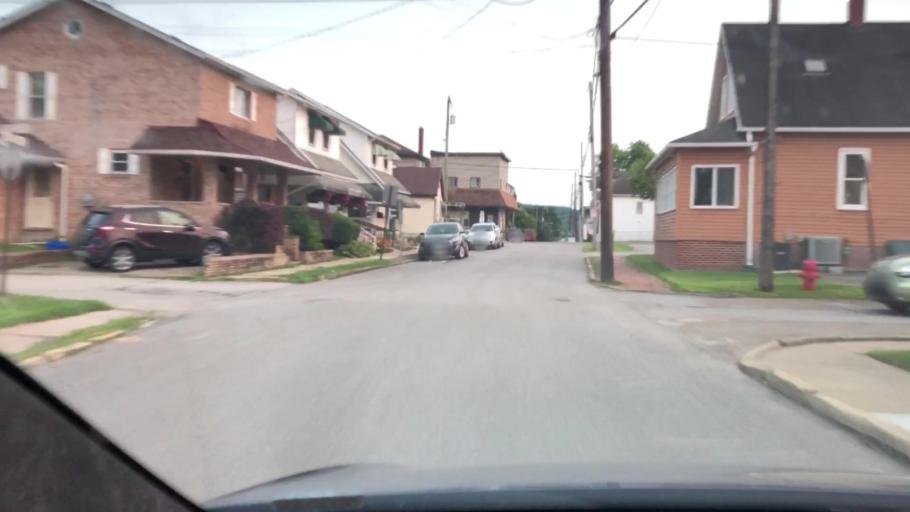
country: US
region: Pennsylvania
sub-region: Butler County
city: Butler
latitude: 40.8636
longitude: -79.9084
